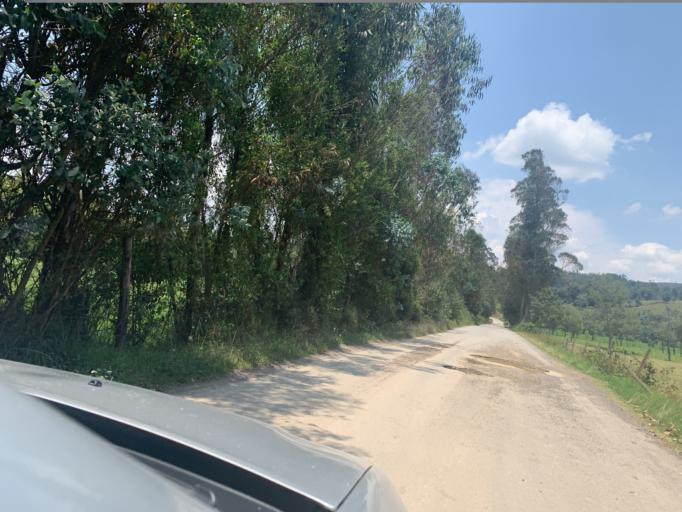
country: CO
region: Boyaca
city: Chiquinquira
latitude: 5.5712
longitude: -73.7473
